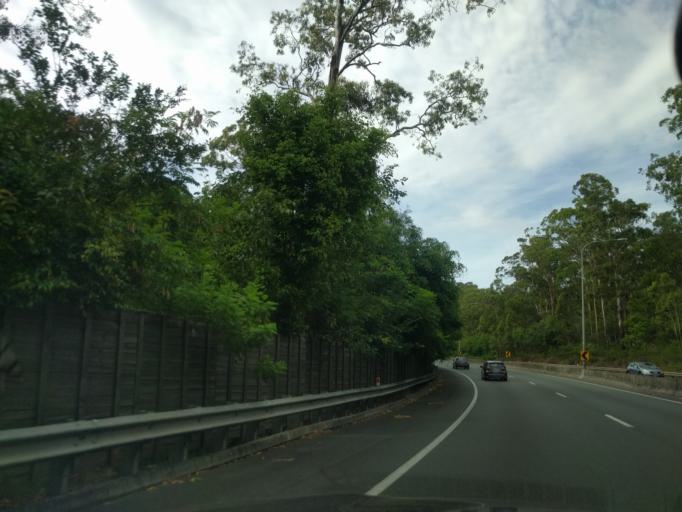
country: AU
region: Queensland
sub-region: Brisbane
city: Kenmore Hills
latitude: -27.5208
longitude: 152.9486
